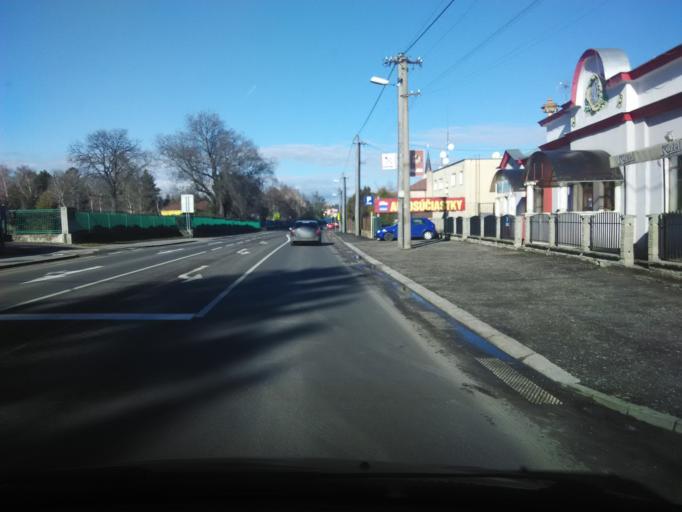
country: SK
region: Nitriansky
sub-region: Okres Nitra
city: Nitra
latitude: 48.2418
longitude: 18.1156
